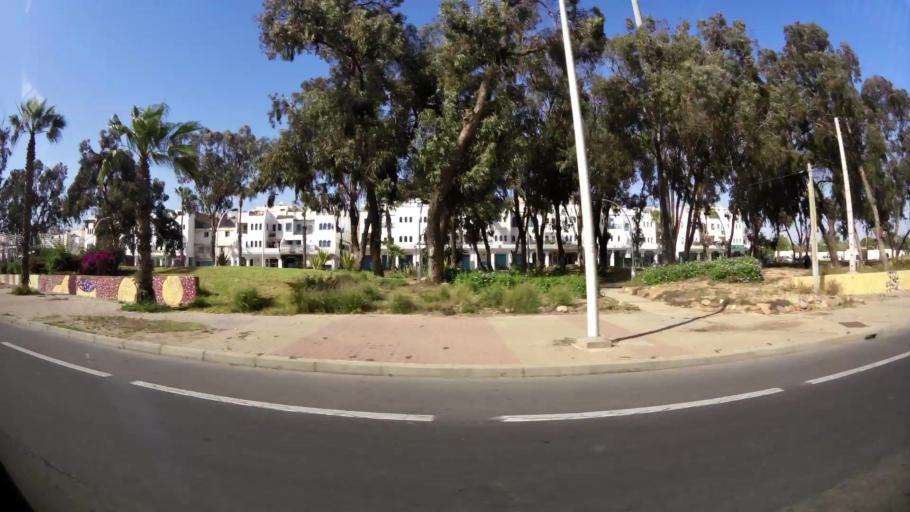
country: MA
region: Oued ed Dahab-Lagouira
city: Dakhla
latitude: 30.3826
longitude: -9.5684
